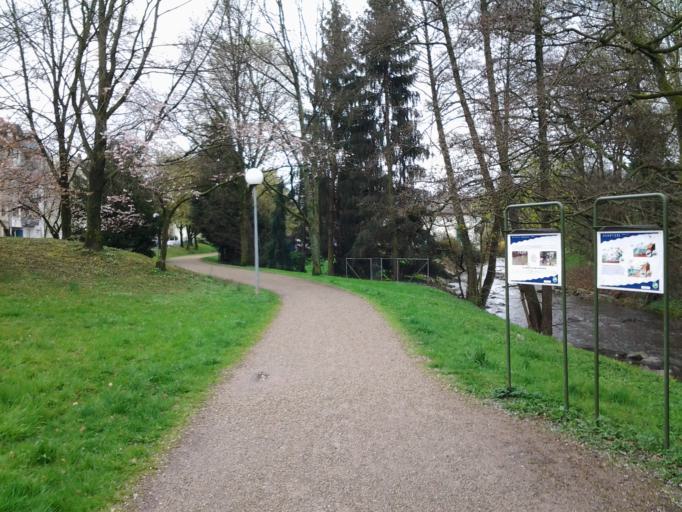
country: DE
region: Baden-Wuerttemberg
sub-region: Karlsruhe Region
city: Baden-Baden
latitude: 48.7742
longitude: 8.2205
